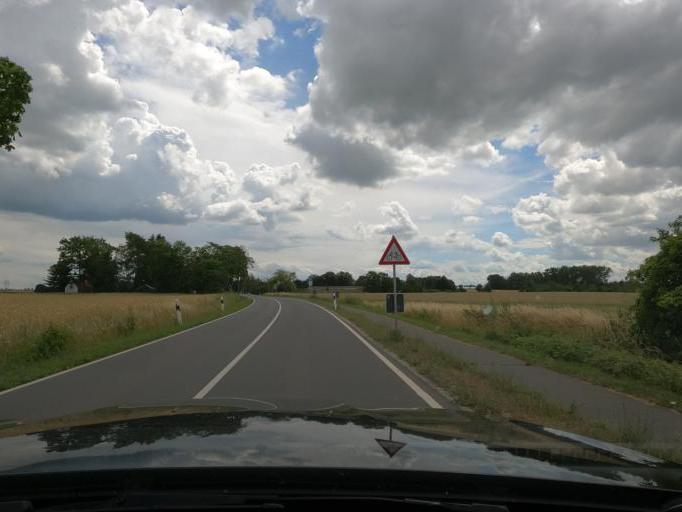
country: DE
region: Lower Saxony
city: Sehnde
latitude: 52.3039
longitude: 9.9792
